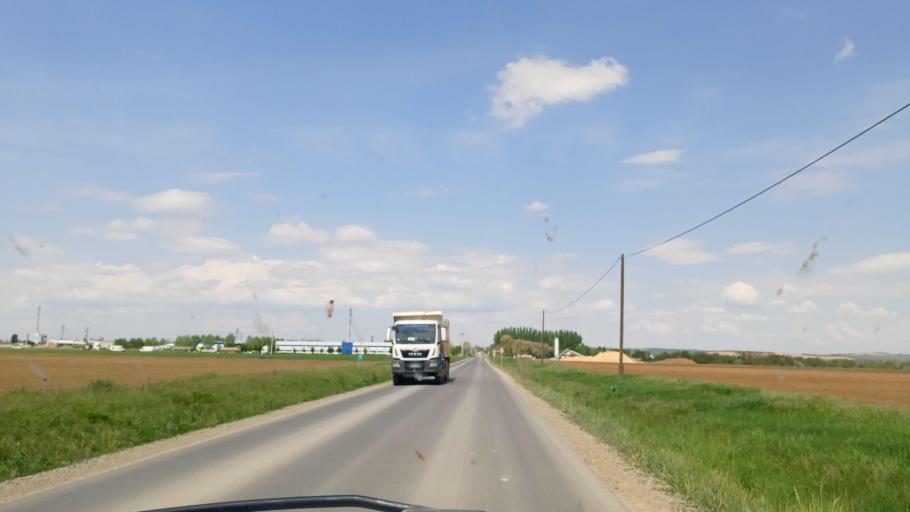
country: HU
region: Baranya
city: Boly
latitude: 45.9516
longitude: 18.5326
